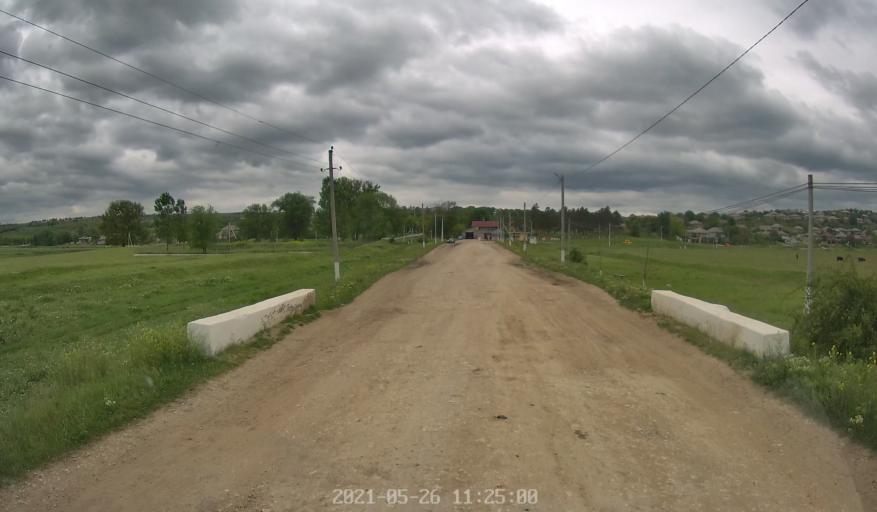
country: MD
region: Hincesti
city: Dancu
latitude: 46.8248
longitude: 28.3718
